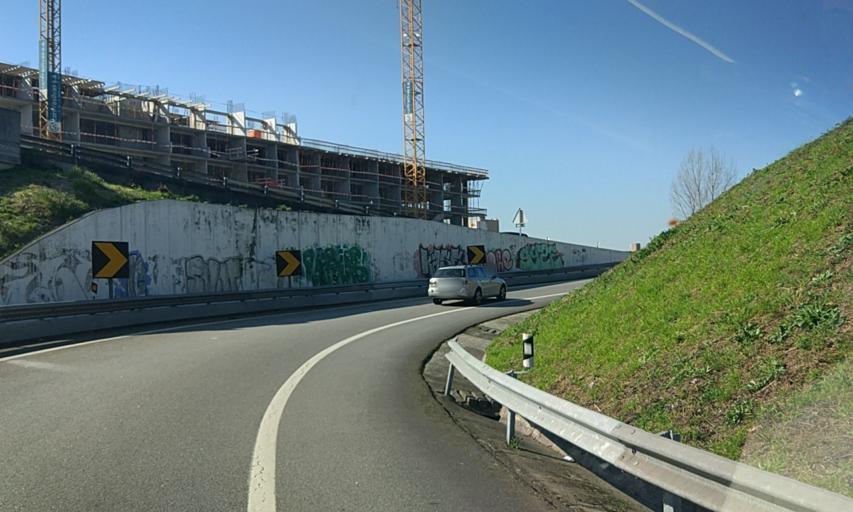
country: PT
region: Porto
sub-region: Matosinhos
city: Senhora da Hora
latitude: 41.1682
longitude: -8.6376
